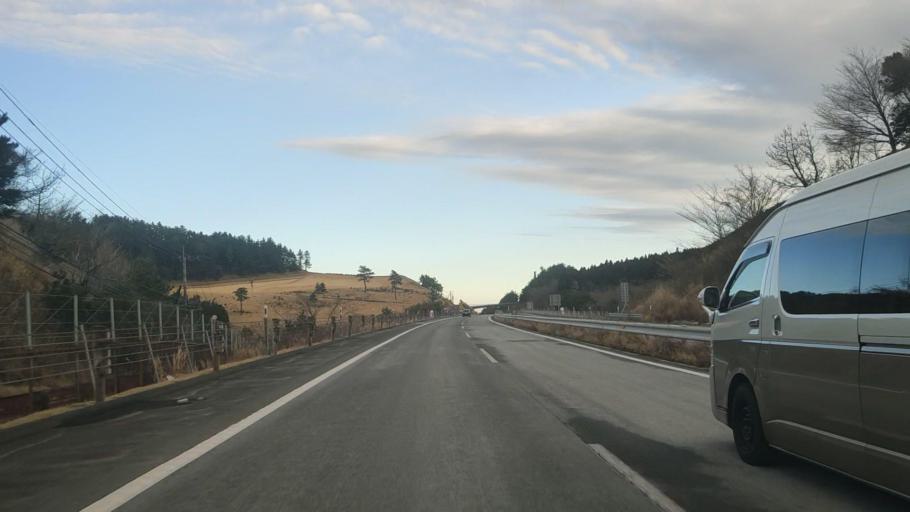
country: JP
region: Oita
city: Beppu
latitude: 33.3161
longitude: 131.4096
